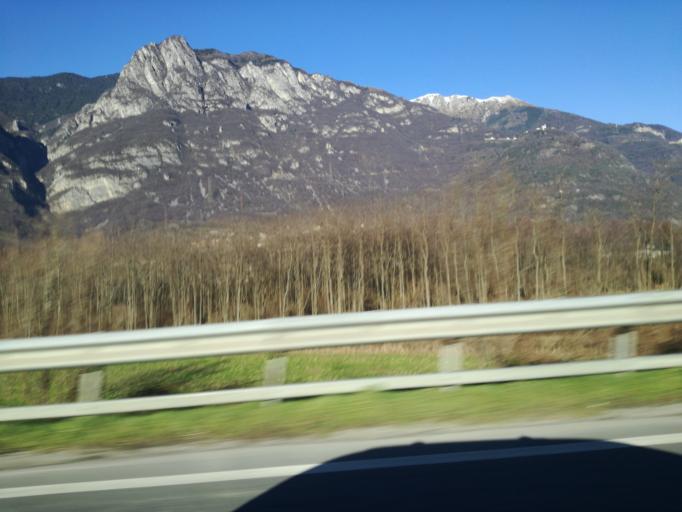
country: IT
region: Lombardy
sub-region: Provincia di Brescia
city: Gratacasolo
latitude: 45.8361
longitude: 10.1182
